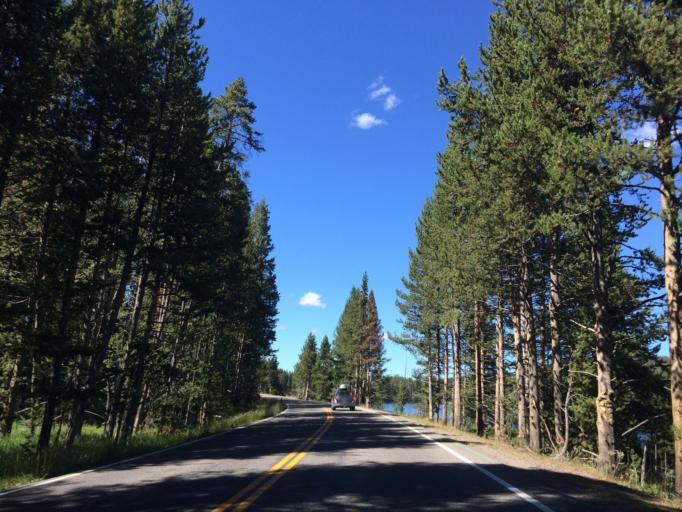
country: US
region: Montana
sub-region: Gallatin County
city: West Yellowstone
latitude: 44.6152
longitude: -110.4147
